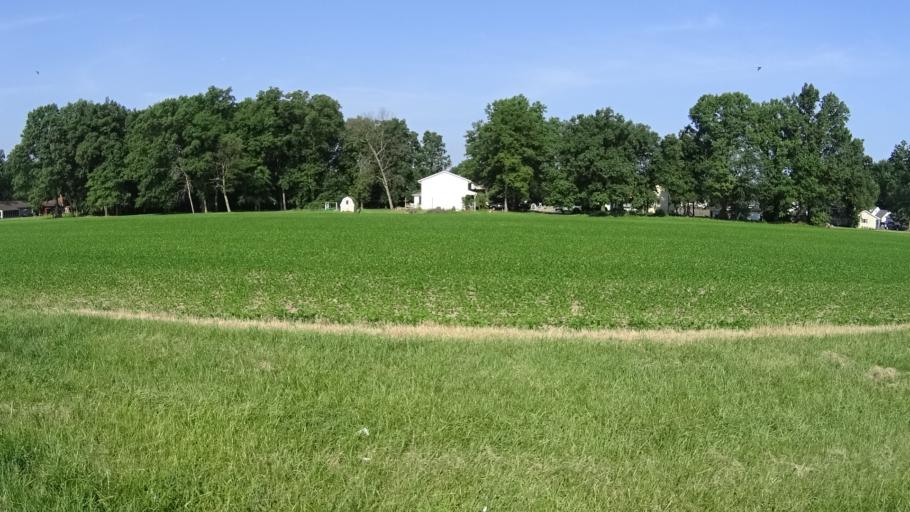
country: US
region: Ohio
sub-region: Lorain County
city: Vermilion
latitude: 41.4126
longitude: -82.3621
